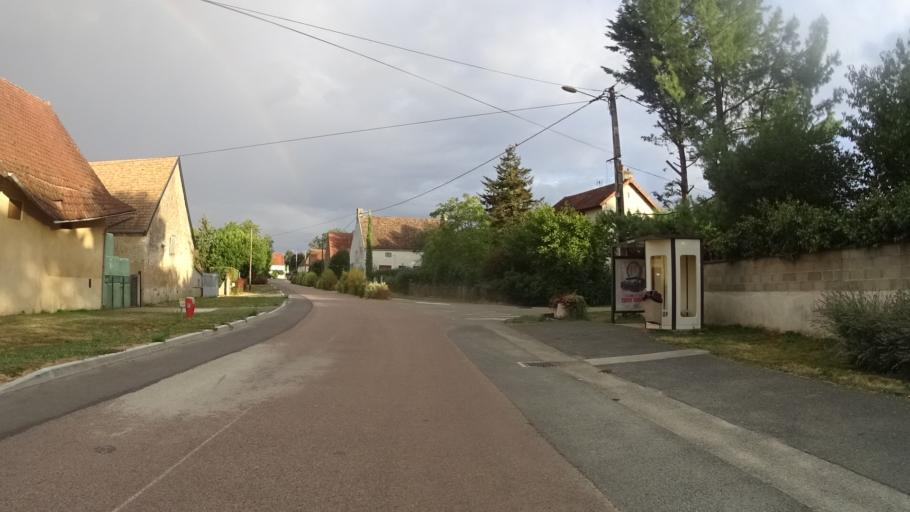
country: FR
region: Bourgogne
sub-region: Departement de Saone-et-Loire
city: Verdun-sur-le-Doubs
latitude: 46.9560
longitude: 5.0320
